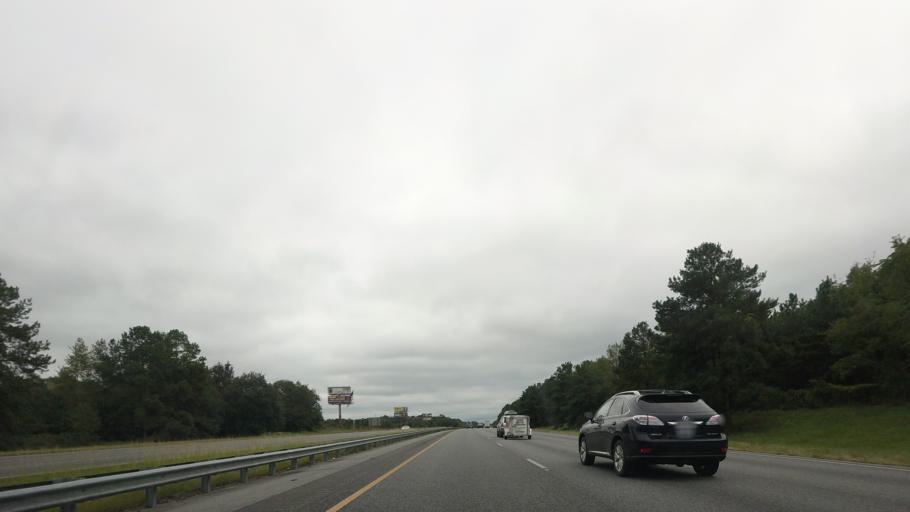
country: US
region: Georgia
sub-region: Lowndes County
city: Valdosta
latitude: 30.8024
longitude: -83.3077
